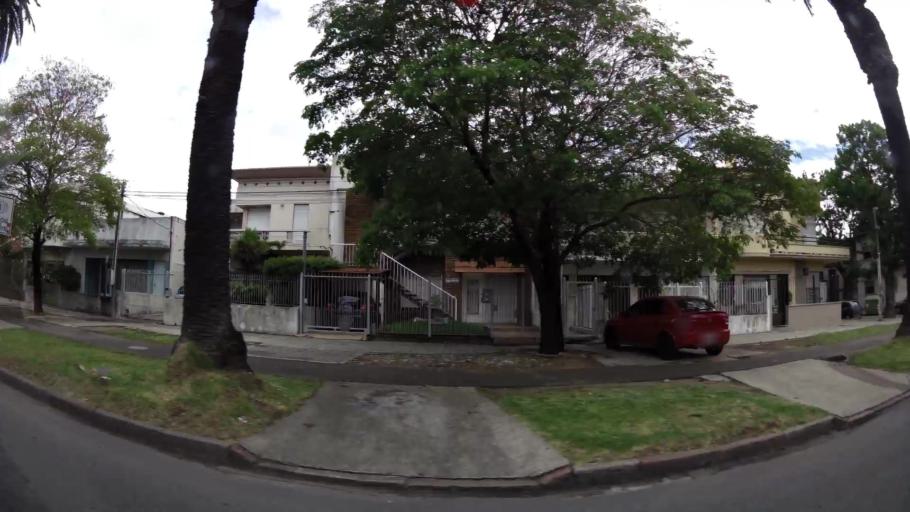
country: UY
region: Montevideo
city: Montevideo
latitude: -34.8709
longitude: -56.1806
